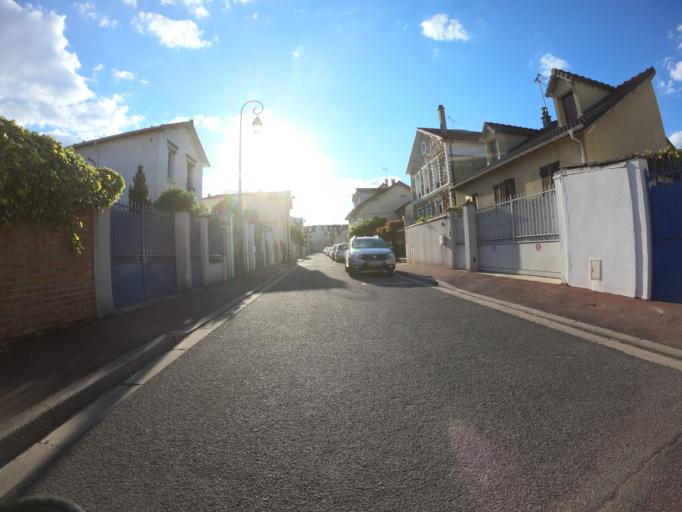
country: FR
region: Ile-de-France
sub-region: Departement des Hauts-de-Seine
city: Antony
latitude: 48.7558
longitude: 2.3081
